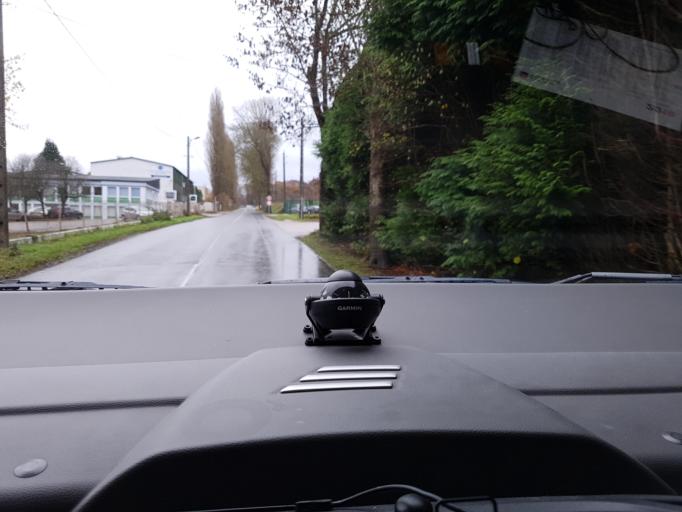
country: FR
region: Haute-Normandie
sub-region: Departement de l'Eure
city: Pont-Saint-Pierre
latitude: 49.3334
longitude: 1.2924
